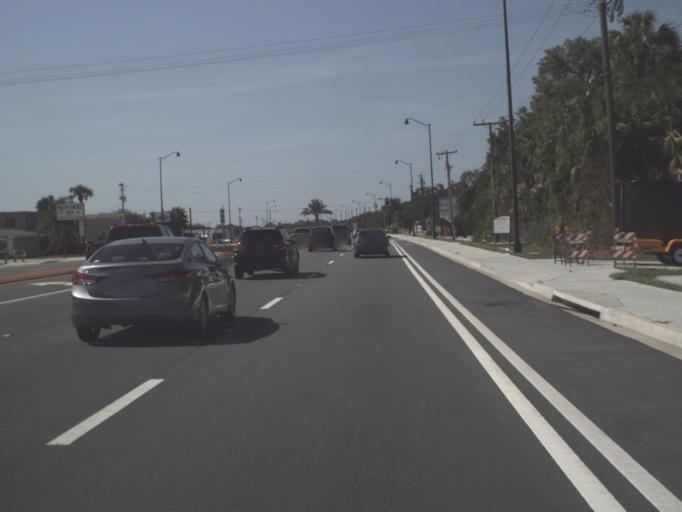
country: US
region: Florida
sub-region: Brevard County
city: Cocoa
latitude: 28.3718
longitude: -80.7357
